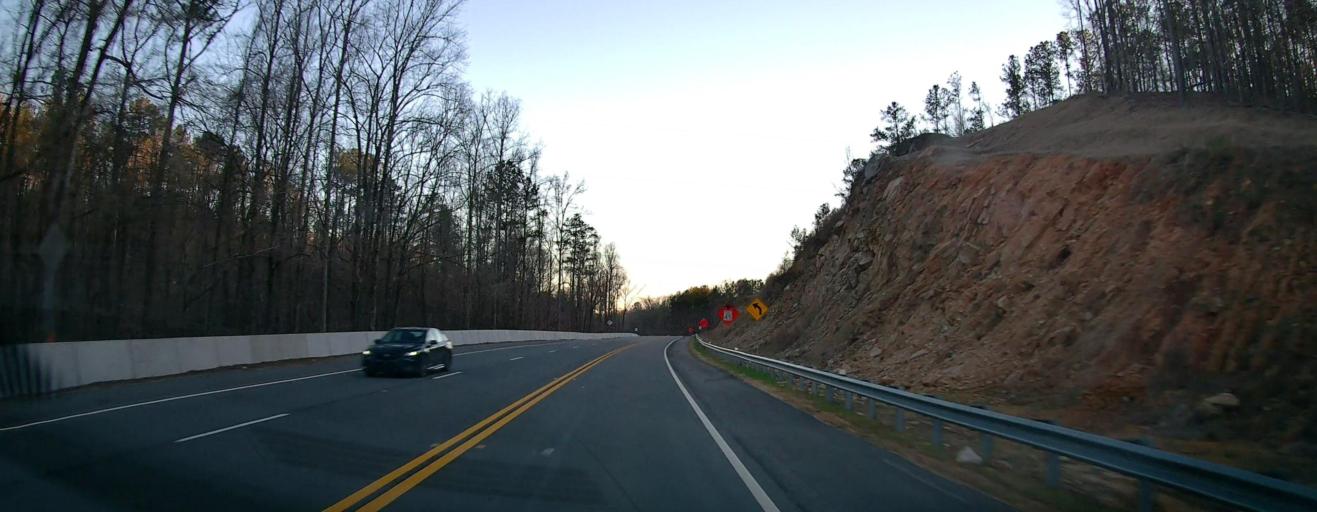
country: US
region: Alabama
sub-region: Lee County
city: Smiths Station
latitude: 32.6137
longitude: -85.0268
